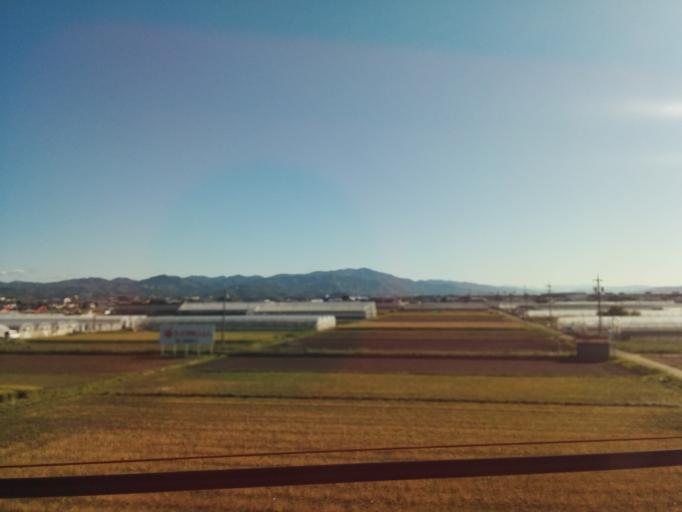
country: JP
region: Aichi
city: Kozakai-cho
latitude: 34.7987
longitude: 137.3273
